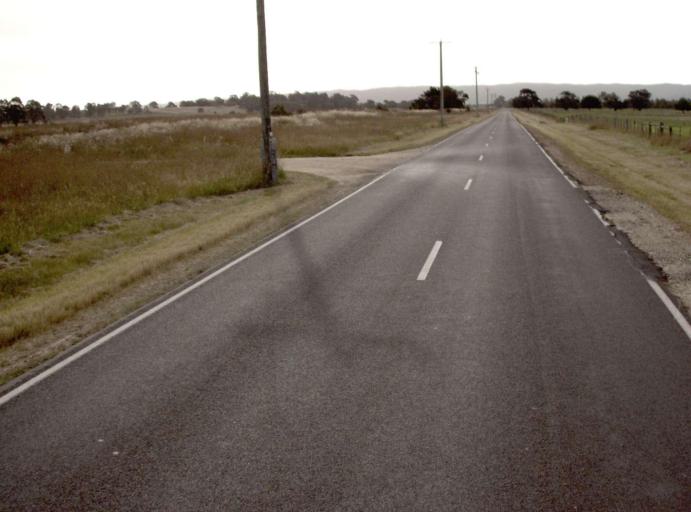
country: AU
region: Victoria
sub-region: Wellington
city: Heyfield
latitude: -38.0196
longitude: 146.7309
